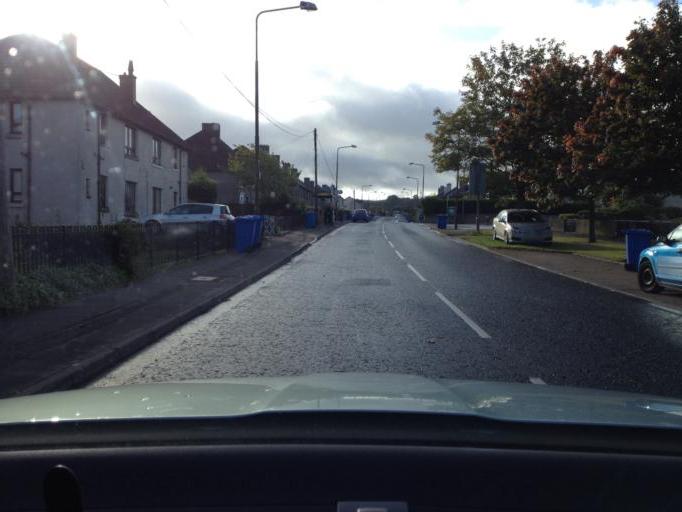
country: GB
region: Scotland
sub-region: West Lothian
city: East Calder
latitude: 55.8924
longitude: -3.4643
